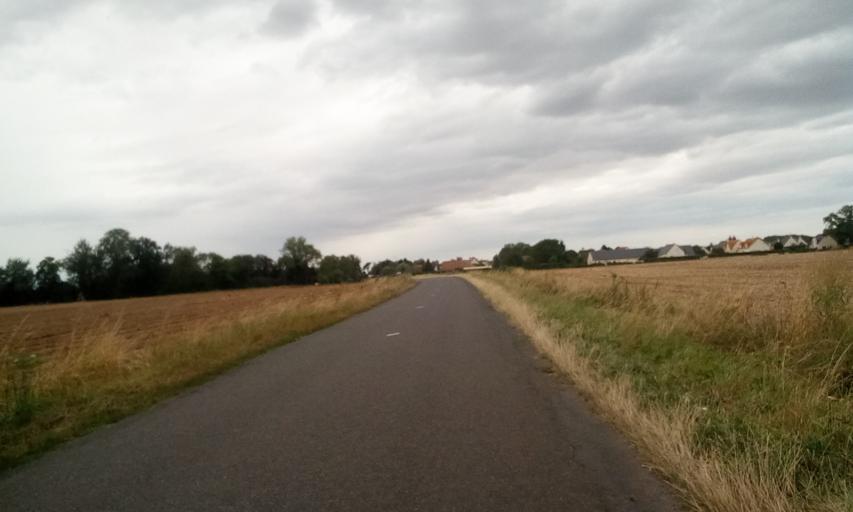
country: FR
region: Lower Normandy
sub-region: Departement du Calvados
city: Bellengreville
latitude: 49.1476
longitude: -0.2191
